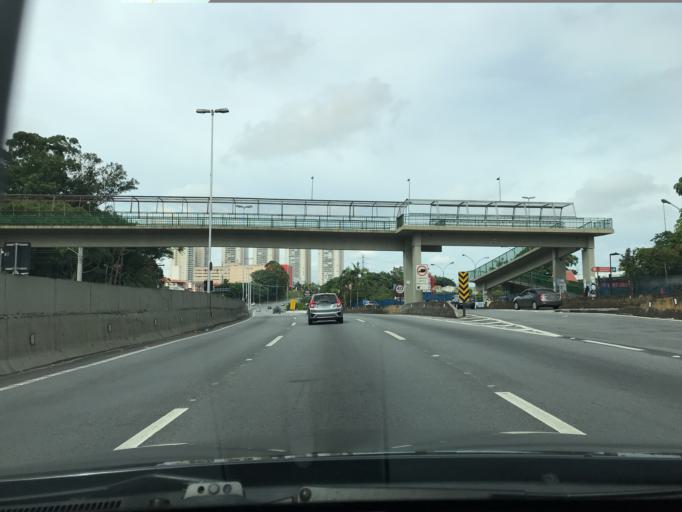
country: BR
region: Sao Paulo
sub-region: Taboao Da Serra
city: Taboao da Serra
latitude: -23.5851
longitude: -46.7458
